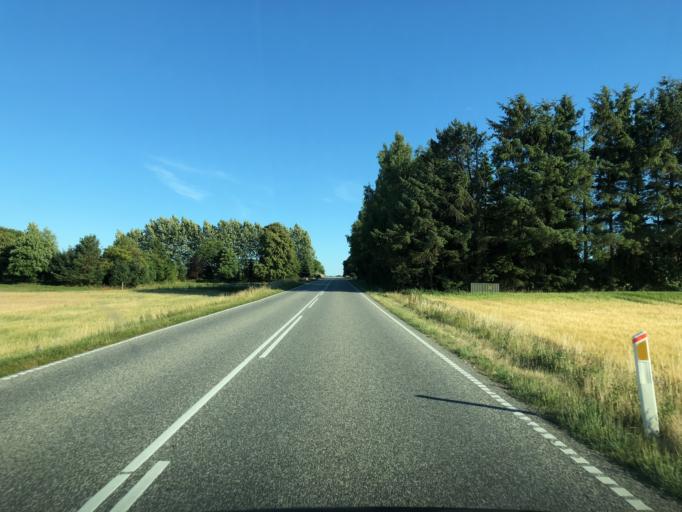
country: DK
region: Central Jutland
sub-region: Skanderborg Kommune
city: Stilling
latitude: 56.0821
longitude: 9.9722
